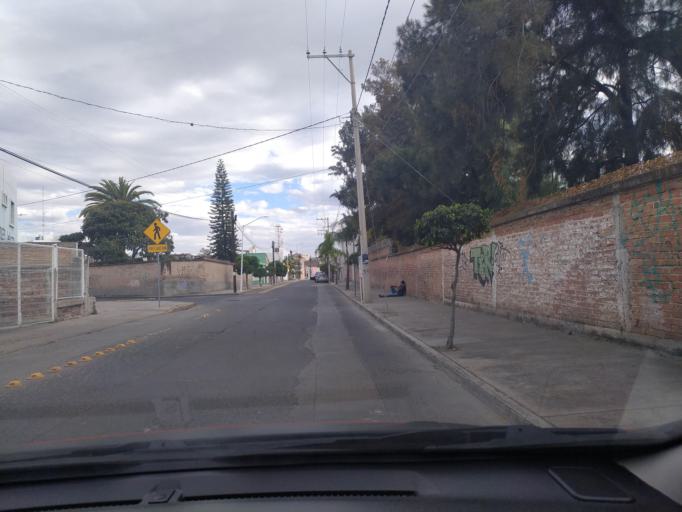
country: LA
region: Oudomxai
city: Muang La
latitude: 21.0198
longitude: 101.8623
